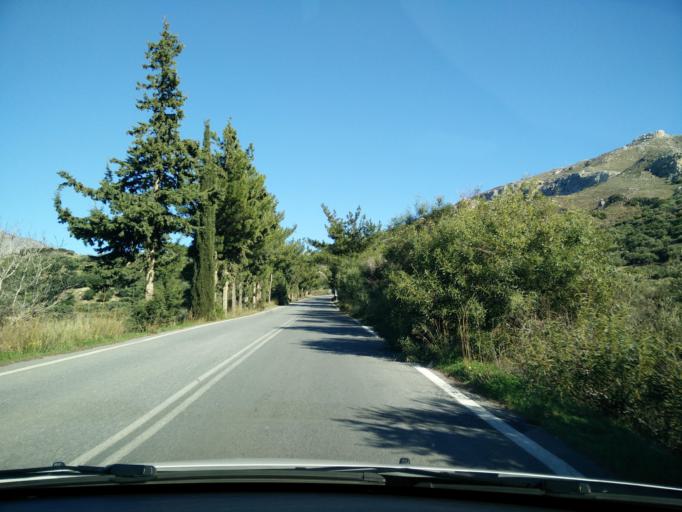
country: GR
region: Crete
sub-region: Nomos Irakleiou
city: Arkalochori
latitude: 35.0781
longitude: 25.3604
